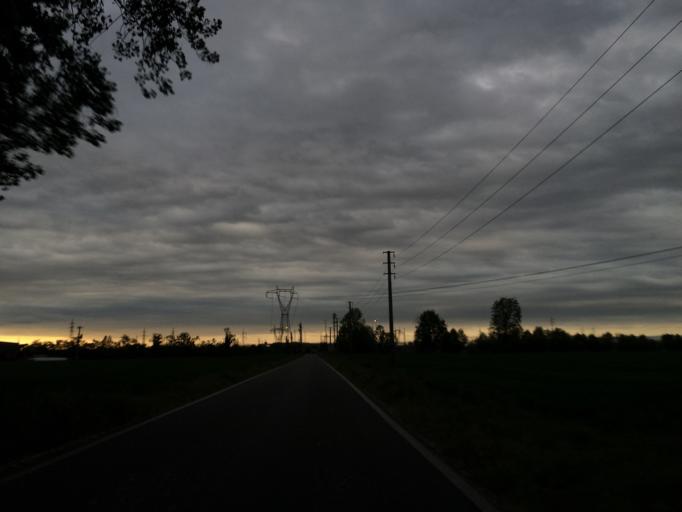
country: IT
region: Lombardy
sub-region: Provincia di Brescia
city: Folzano
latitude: 45.4975
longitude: 10.1885
